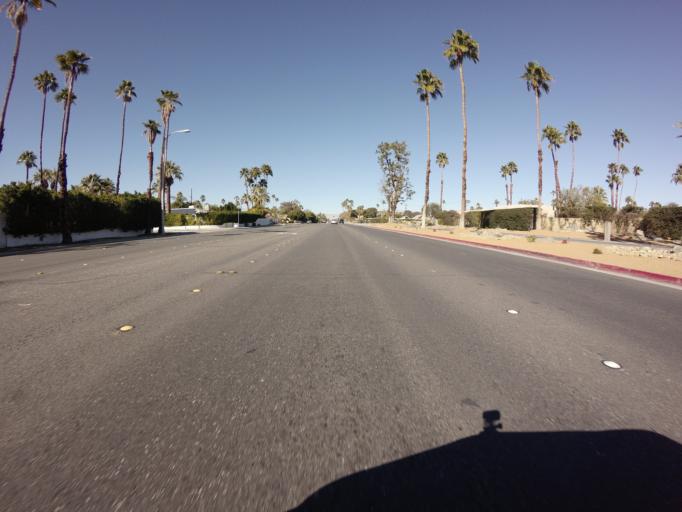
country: US
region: California
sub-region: Riverside County
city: Palm Springs
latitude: 33.8353
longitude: -116.5282
